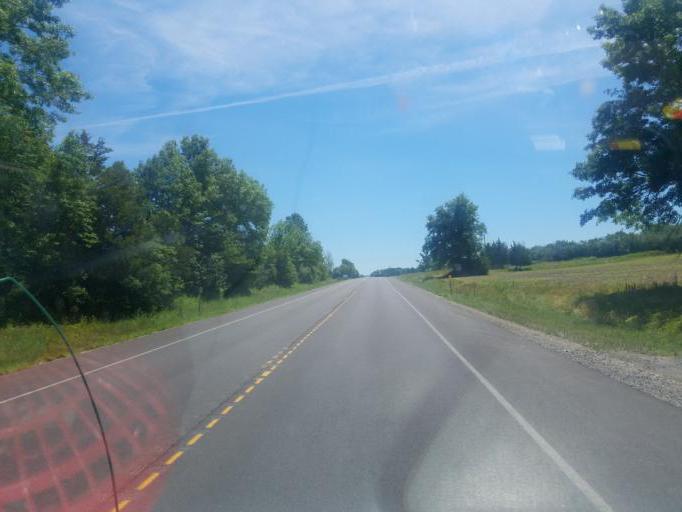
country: US
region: New York
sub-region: Yates County
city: Dundee
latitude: 42.5806
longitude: -76.9327
